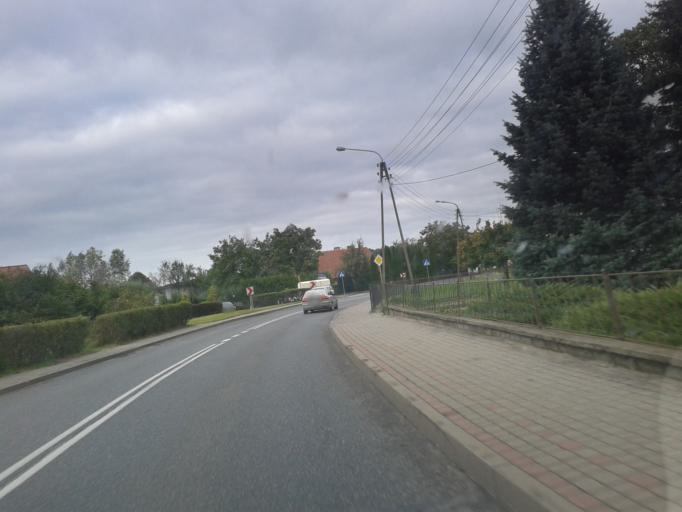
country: PL
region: Kujawsko-Pomorskie
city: Kamien Krajenski
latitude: 53.5323
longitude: 17.5141
